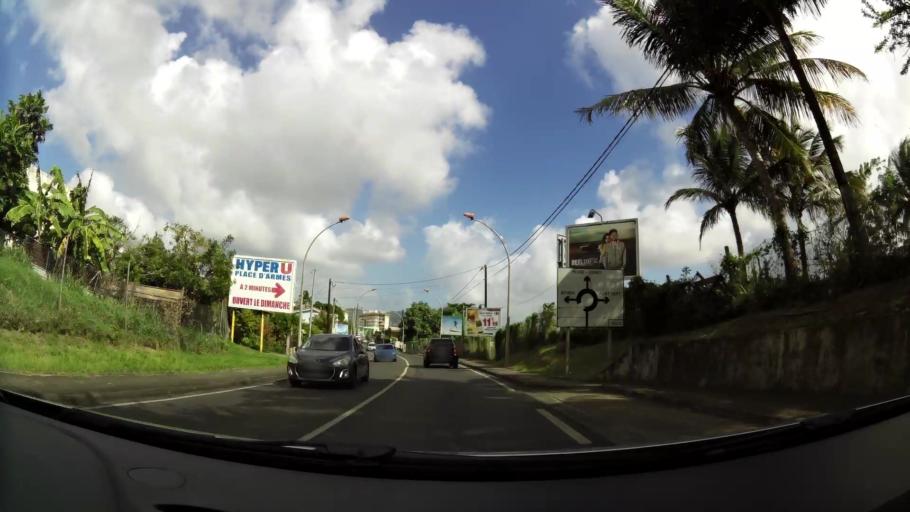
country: MQ
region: Martinique
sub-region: Martinique
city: Le Lamentin
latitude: 14.6104
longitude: -61.0031
